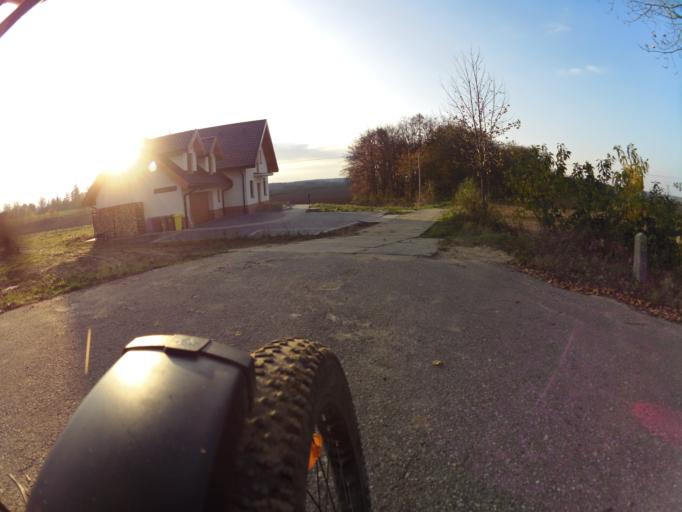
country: PL
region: Pomeranian Voivodeship
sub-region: Powiat pucki
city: Krokowa
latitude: 54.7699
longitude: 18.1788
